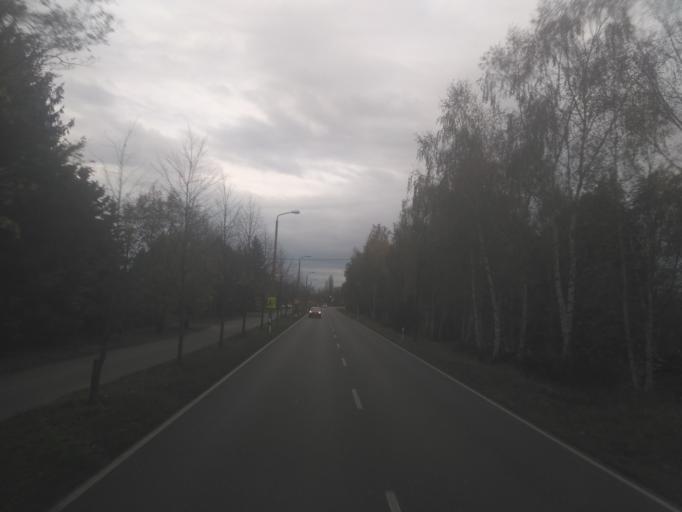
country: DE
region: Brandenburg
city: Elsterwerda
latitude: 51.4652
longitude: 13.5042
